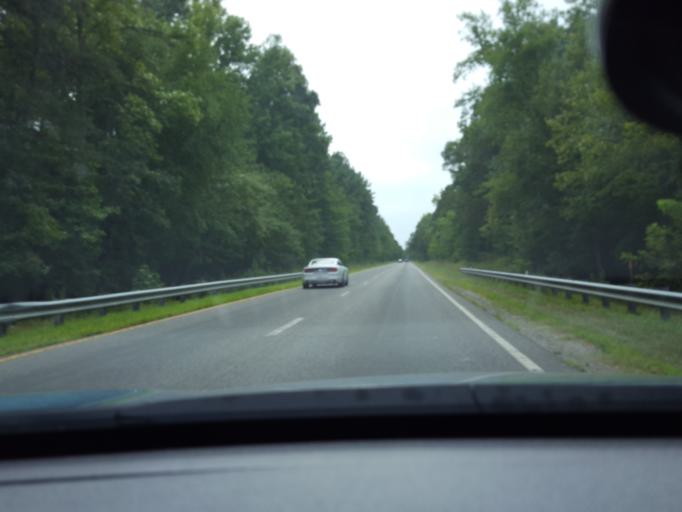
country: US
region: Virginia
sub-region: Caroline County
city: Bowling Green
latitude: 38.1221
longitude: -77.2494
